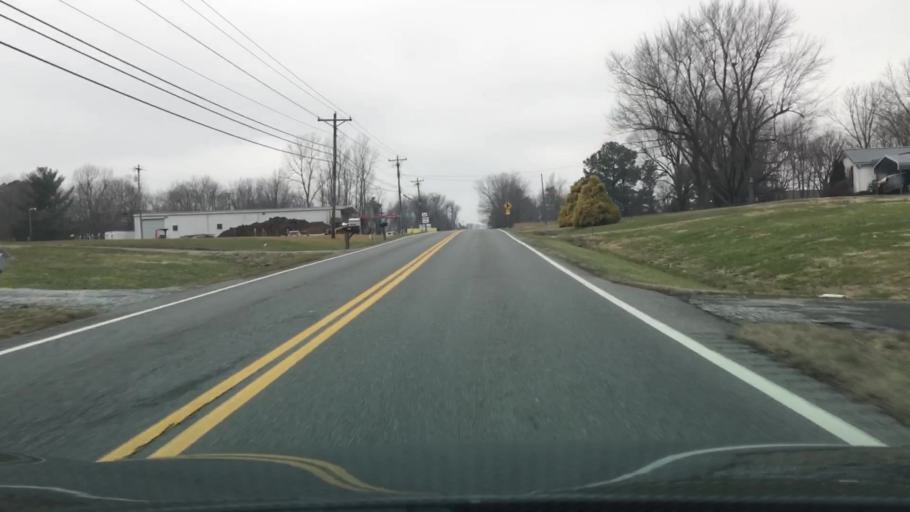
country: US
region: Kentucky
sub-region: McCracken County
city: Reidland
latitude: 36.9859
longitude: -88.4976
